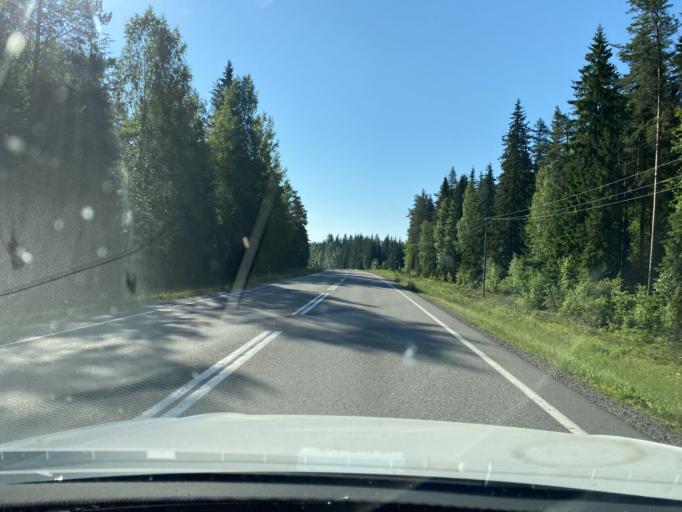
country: FI
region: Haeme
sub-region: Riihimaeki
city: Loppi
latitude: 60.7518
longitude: 24.3097
